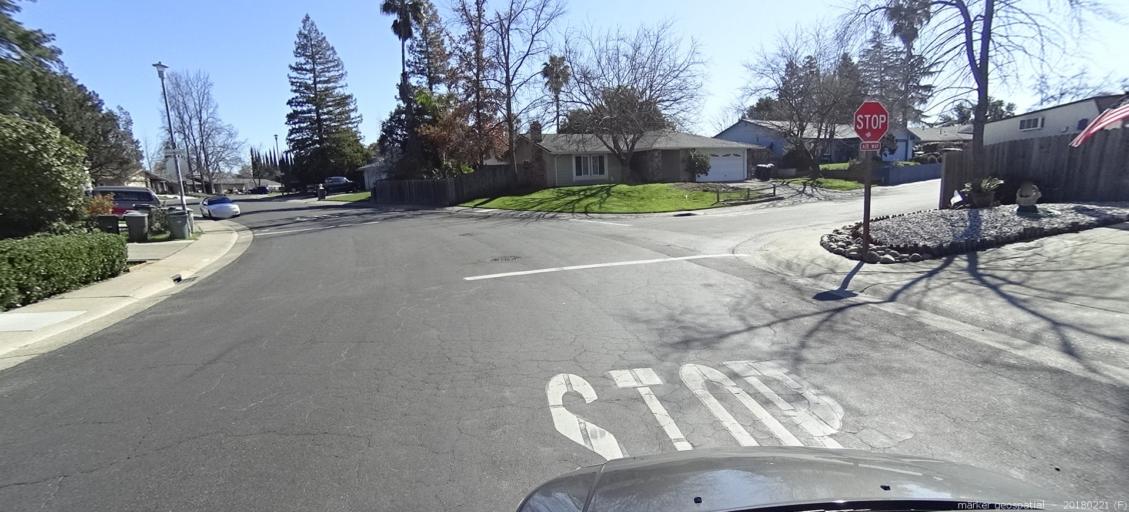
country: US
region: California
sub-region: Sacramento County
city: Orangevale
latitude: 38.6908
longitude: -121.2530
